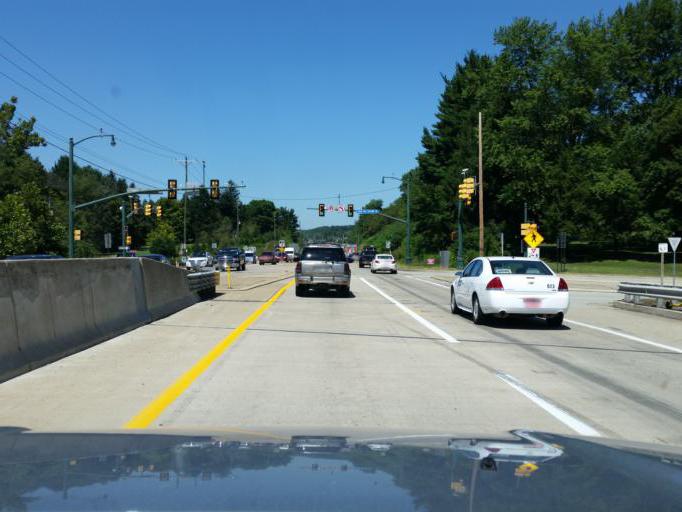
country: US
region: Pennsylvania
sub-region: Westmoreland County
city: Murrysville
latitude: 40.4194
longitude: -79.6530
